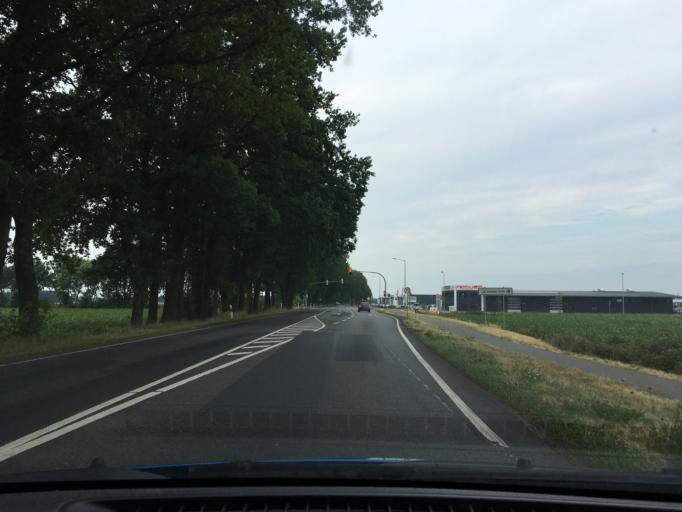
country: DE
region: Lower Saxony
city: Tostedt
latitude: 53.2873
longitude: 9.7233
